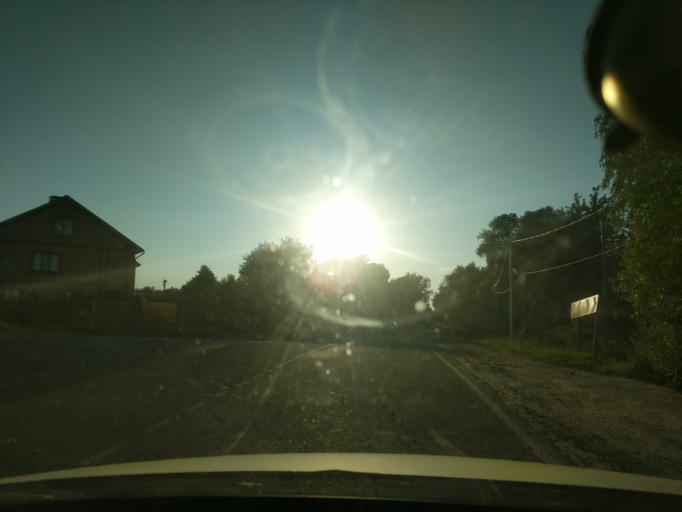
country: RU
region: Moskovskaya
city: Serpukhov
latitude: 54.8601
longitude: 37.4764
